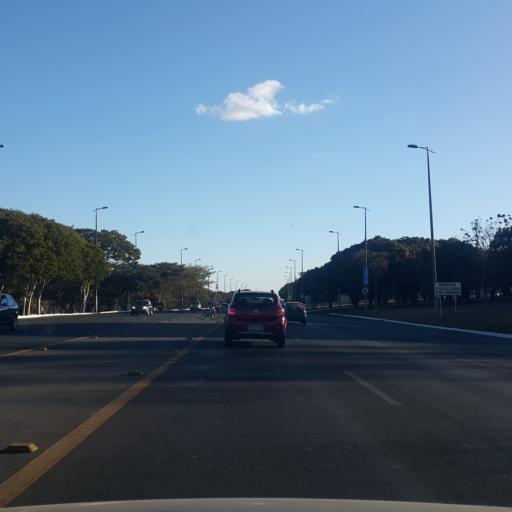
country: BR
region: Federal District
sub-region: Brasilia
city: Brasilia
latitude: -15.8132
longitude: -47.8961
